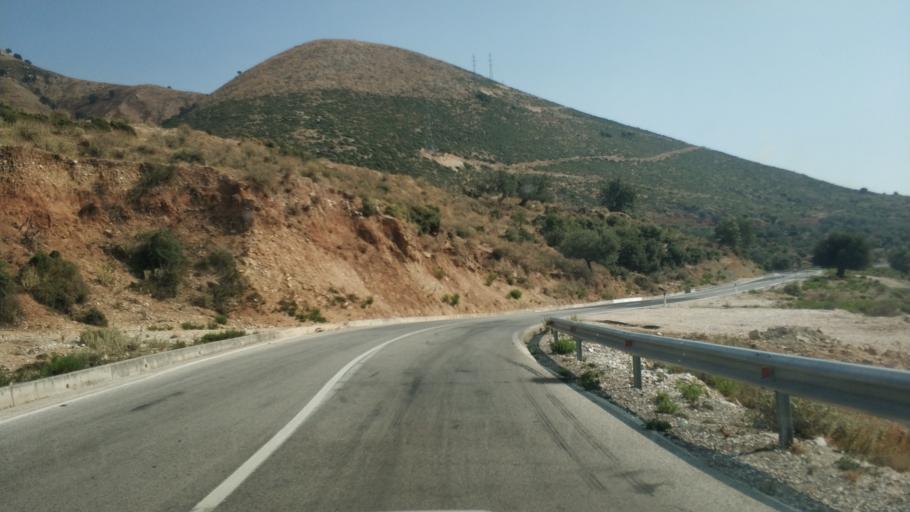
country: AL
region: Vlore
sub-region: Rrethi i Sarandes
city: Lukove
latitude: 40.0342
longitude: 19.8863
